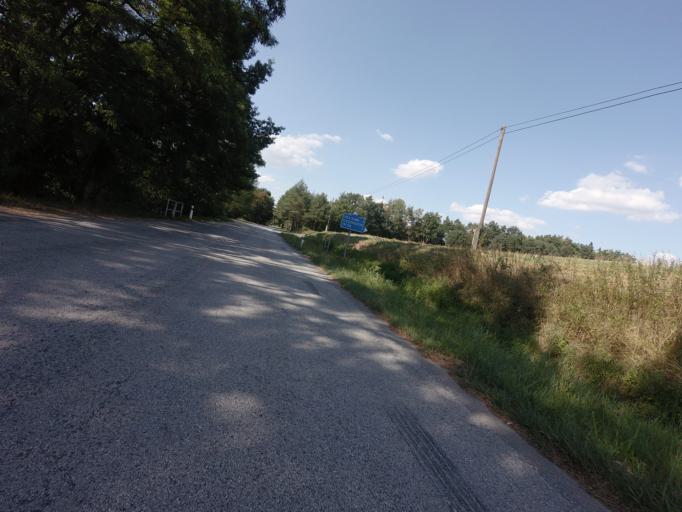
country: CZ
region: Jihocesky
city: Tyn nad Vltavou
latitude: 49.1988
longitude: 14.4459
